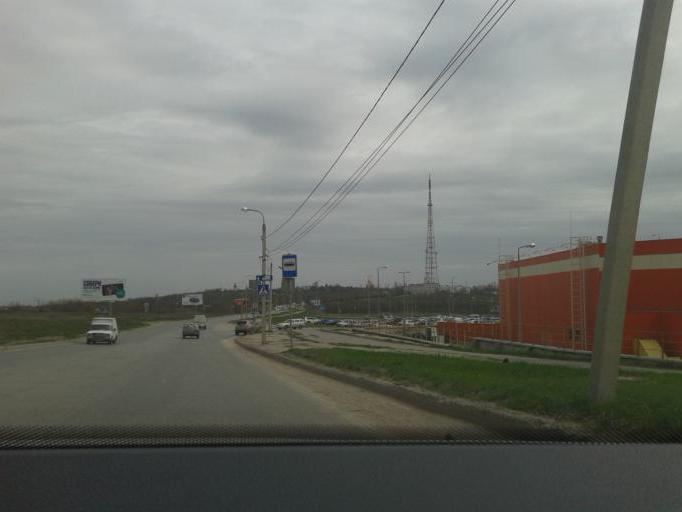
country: RU
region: Volgograd
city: Volgograd
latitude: 48.7461
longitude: 44.5181
